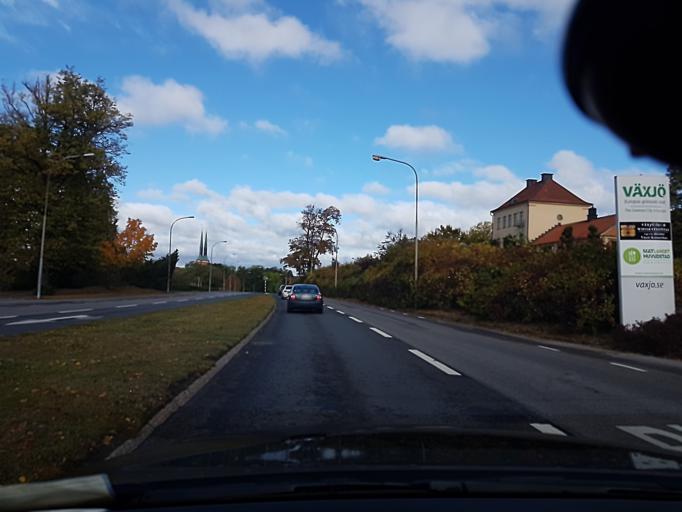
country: SE
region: Kronoberg
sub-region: Vaxjo Kommun
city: Vaexjoe
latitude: 56.8733
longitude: 14.8181
